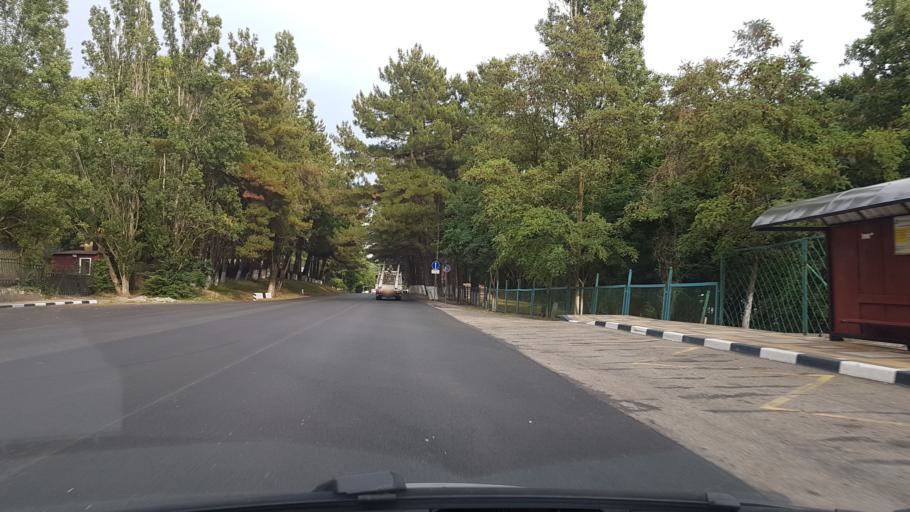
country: RU
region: Krasnodarskiy
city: Lermontovo
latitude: 44.2845
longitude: 38.7856
